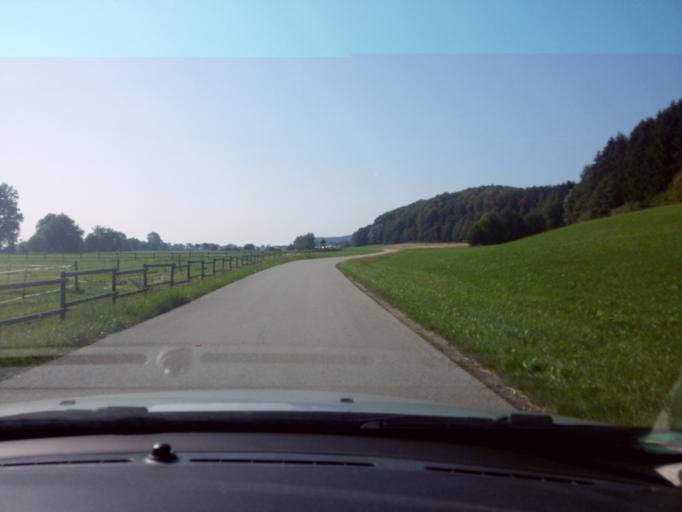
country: DE
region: Bavaria
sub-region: Swabia
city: Hiltenfingen
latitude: 48.1961
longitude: 10.6997
